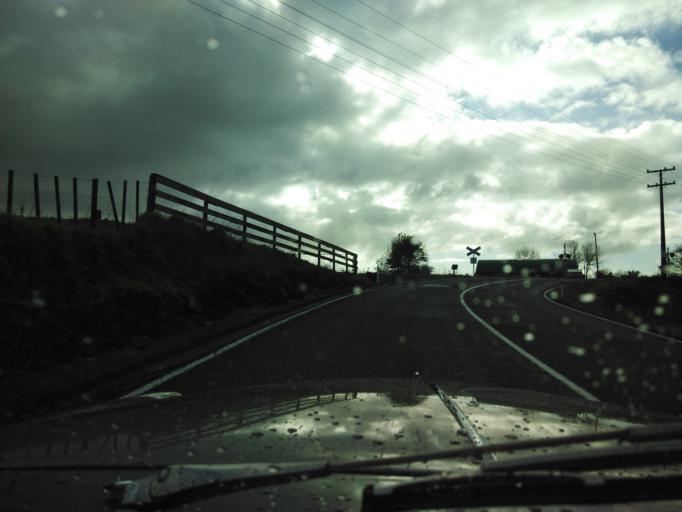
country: NZ
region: Auckland
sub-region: Auckland
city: Wellsford
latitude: -36.1652
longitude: 174.4277
